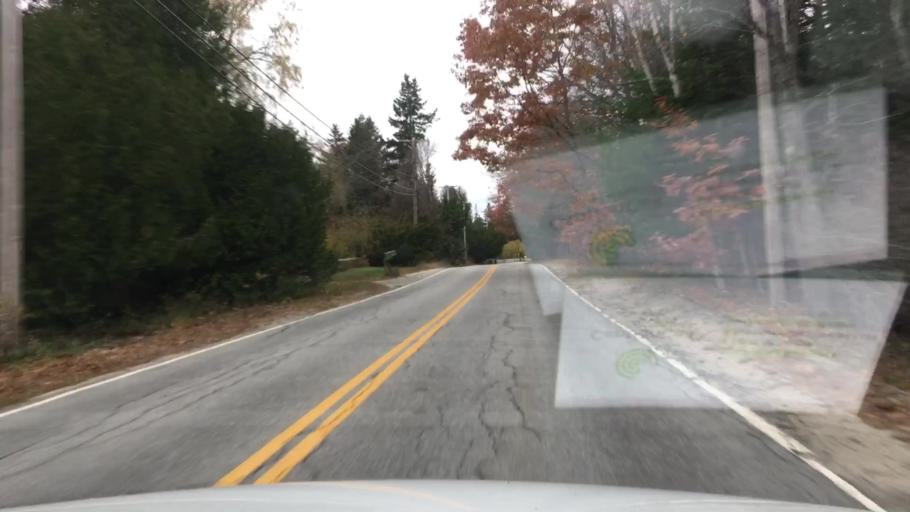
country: US
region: Maine
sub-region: Hancock County
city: Sedgwick
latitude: 44.3693
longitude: -68.5560
